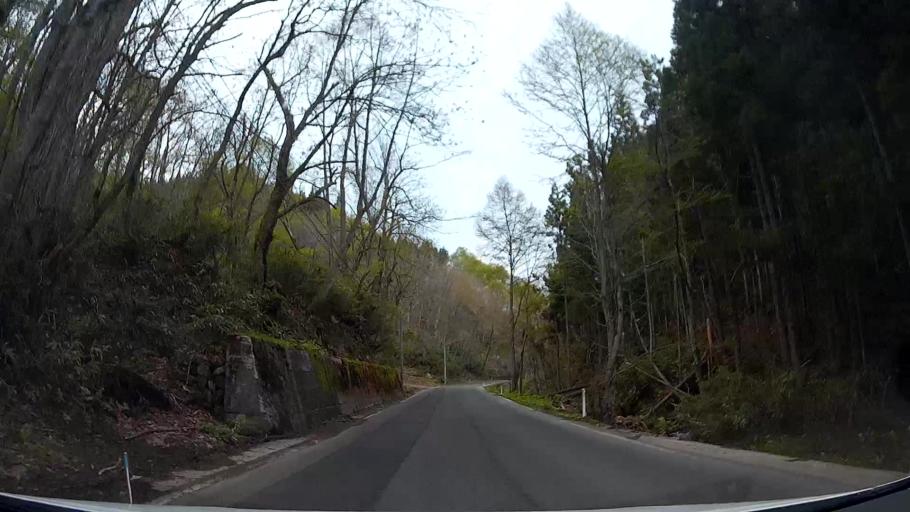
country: JP
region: Akita
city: Hanawa
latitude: 40.3813
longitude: 140.8890
